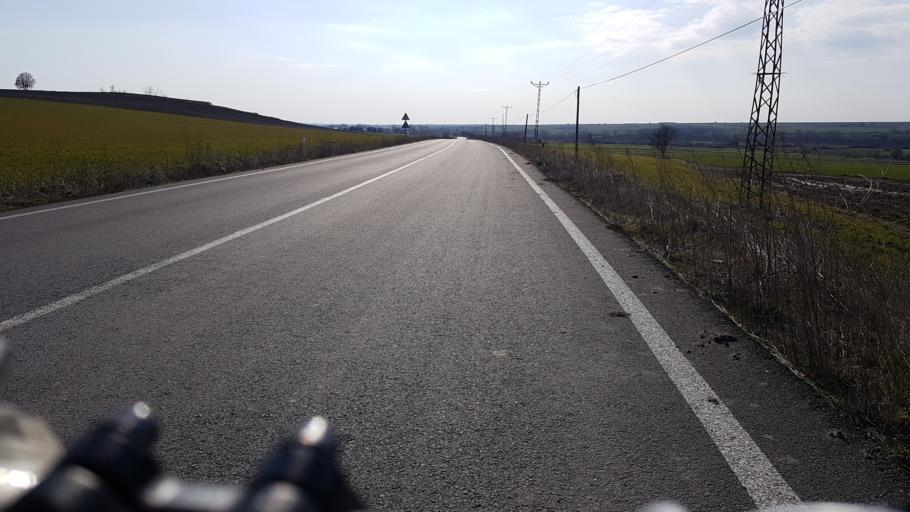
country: TR
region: Tekirdag
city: Velimese
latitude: 41.3543
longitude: 27.8467
